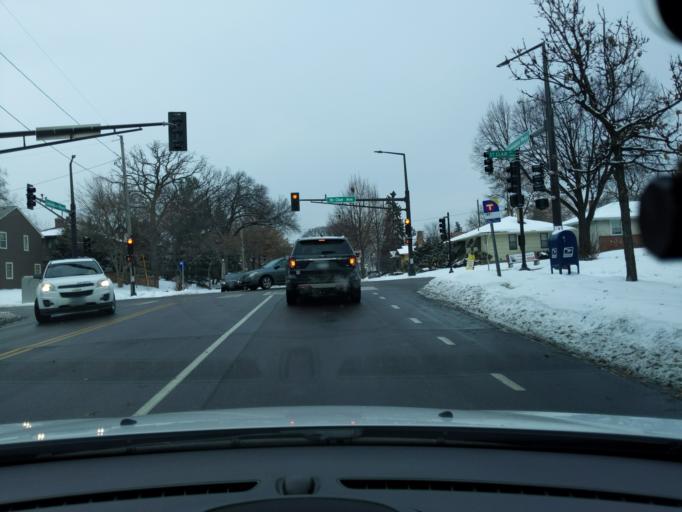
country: US
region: Minnesota
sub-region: Dakota County
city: West Saint Paul
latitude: 44.9339
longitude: -93.1465
